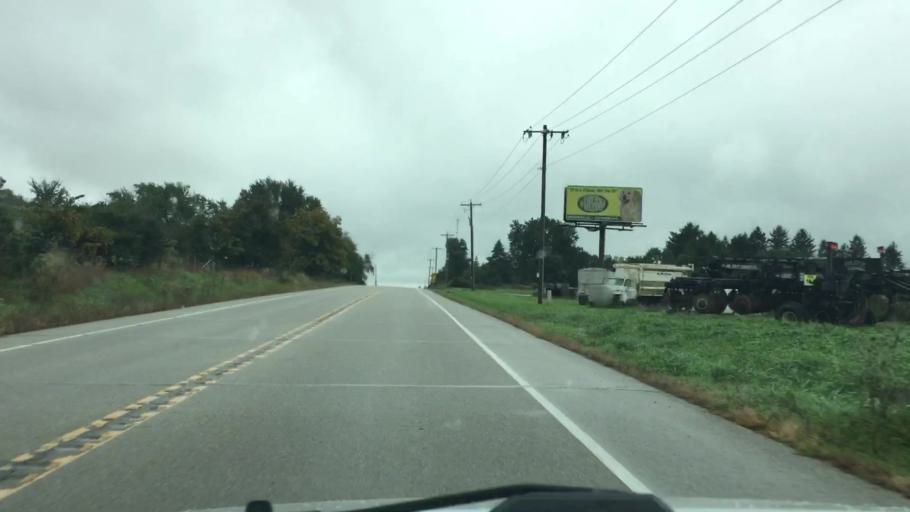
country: US
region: Wisconsin
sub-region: Walworth County
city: Whitewater
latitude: 42.8184
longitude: -88.7523
